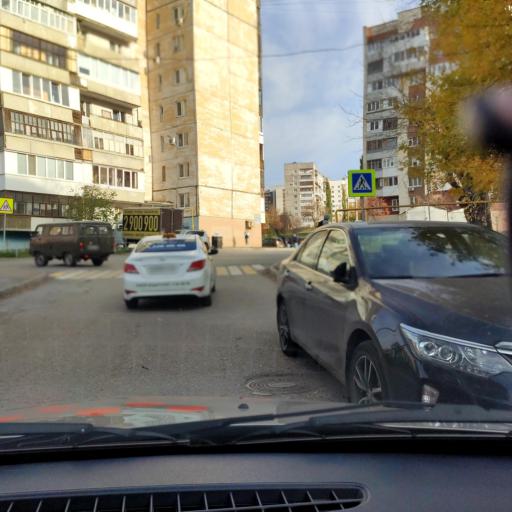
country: RU
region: Bashkortostan
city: Ufa
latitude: 54.7089
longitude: 55.9938
